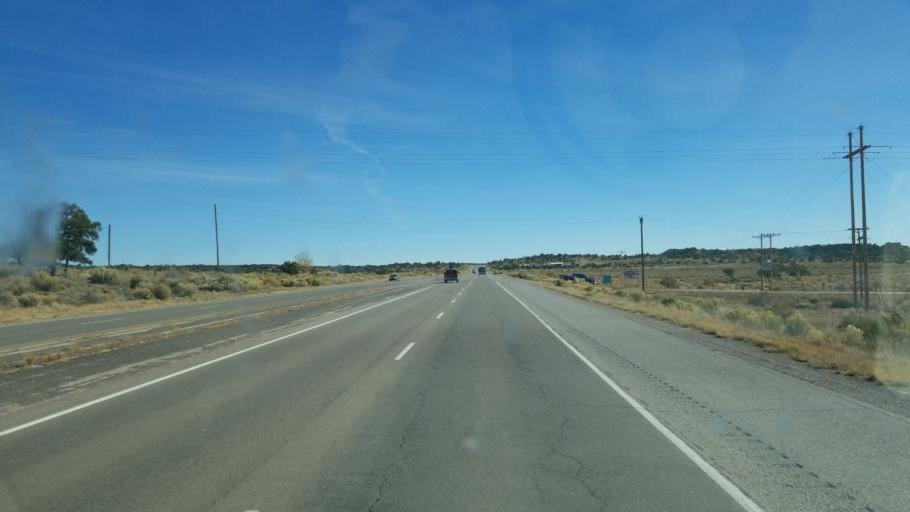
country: US
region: Arizona
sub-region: Apache County
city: Window Rock
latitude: 35.6295
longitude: -108.9202
